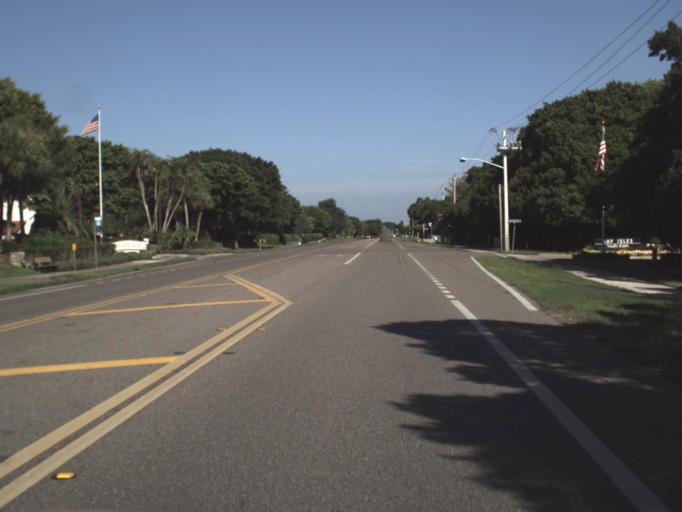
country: US
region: Florida
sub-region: Manatee County
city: Whitfield
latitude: 27.3548
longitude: -82.6126
